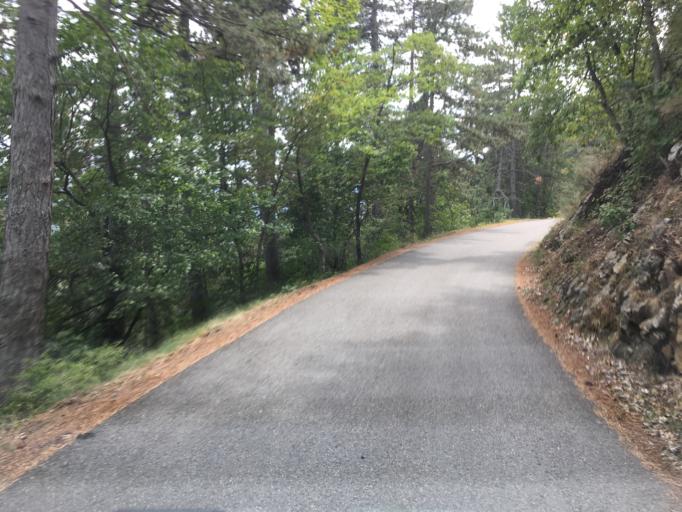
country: FR
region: Provence-Alpes-Cote d'Azur
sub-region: Departement des Alpes-de-Haute-Provence
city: Digne-les-Bains
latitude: 44.2098
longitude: 6.1507
